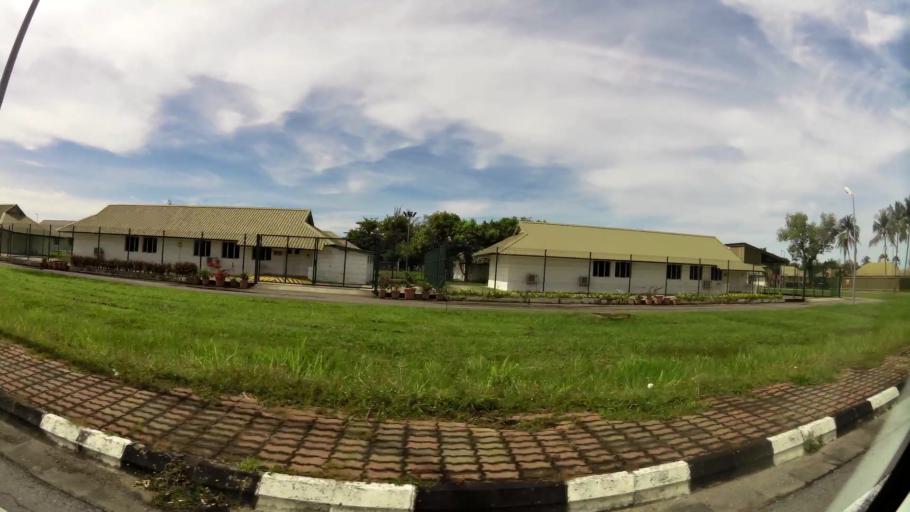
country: BN
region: Belait
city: Seria
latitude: 4.6109
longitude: 114.3156
